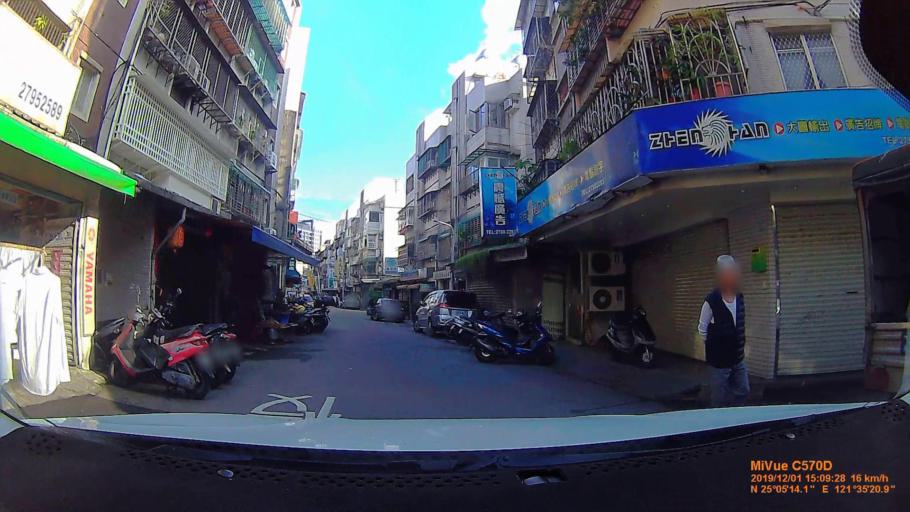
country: TW
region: Taipei
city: Taipei
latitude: 25.0874
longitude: 121.5890
